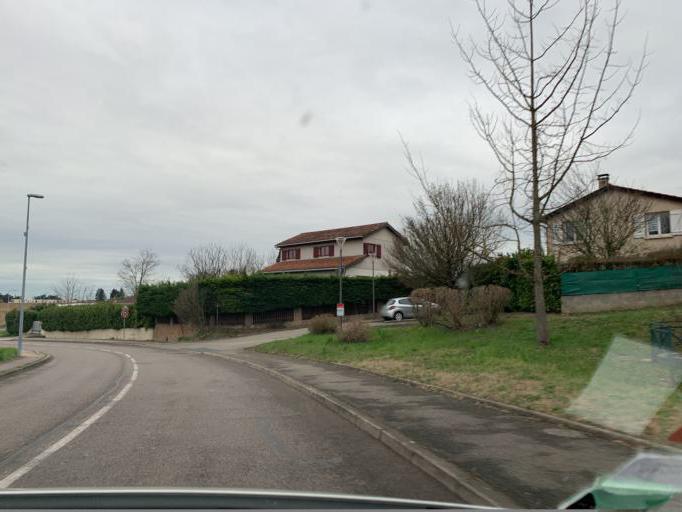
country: FR
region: Rhone-Alpes
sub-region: Departement du Rhone
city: Rillieux-la-Pape
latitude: 45.8314
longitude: 4.9082
